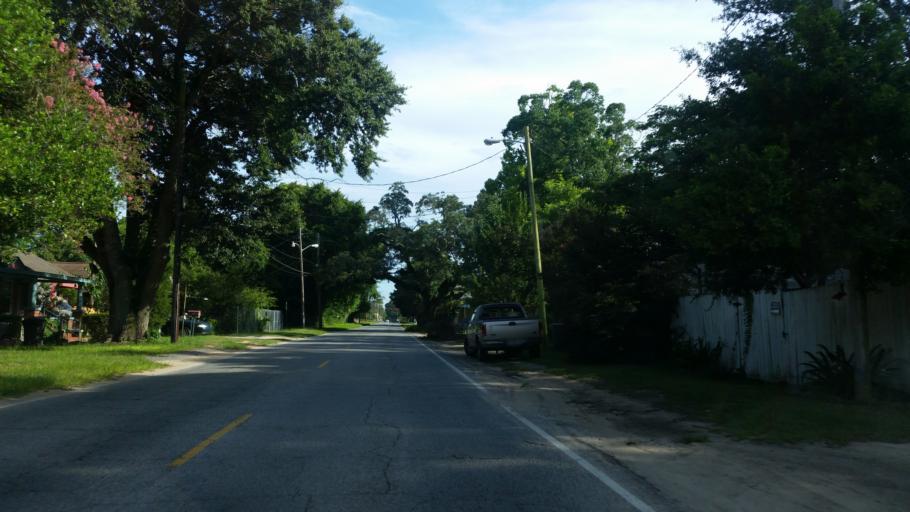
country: US
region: Florida
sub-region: Escambia County
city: Pensacola
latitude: 30.4246
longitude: -87.2467
